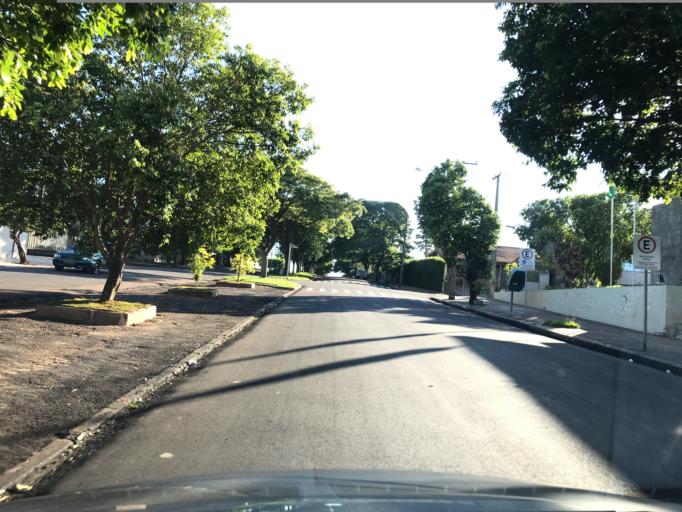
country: BR
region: Parana
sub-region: Ipora
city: Ipora
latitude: -24.0014
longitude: -53.7143
